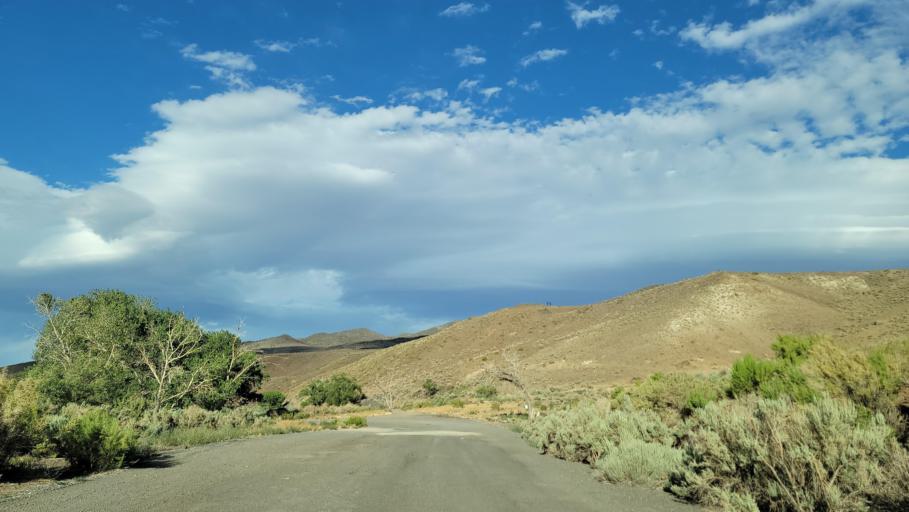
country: US
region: Nevada
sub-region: Washoe County
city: Sparks
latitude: 39.5092
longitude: -119.6279
